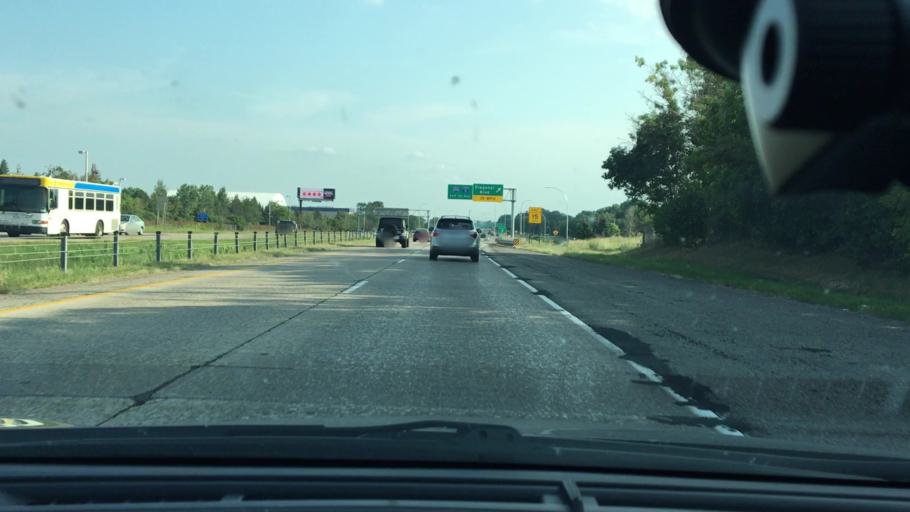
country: US
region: Minnesota
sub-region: Hennepin County
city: Richfield
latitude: 44.8785
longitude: -93.2471
